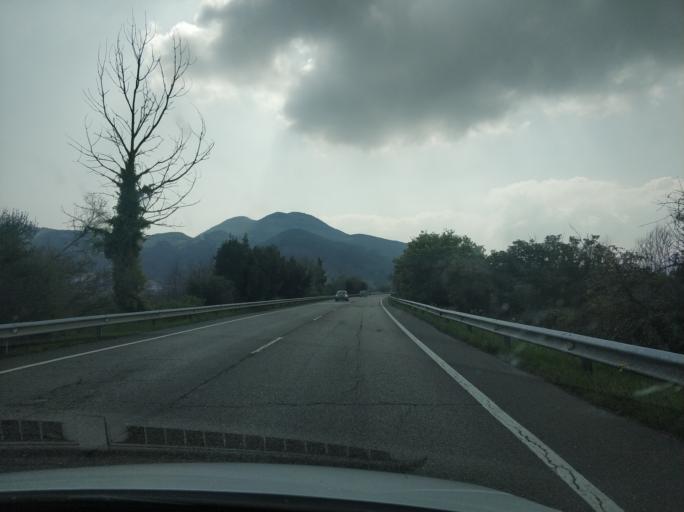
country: ES
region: Cantabria
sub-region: Provincia de Cantabria
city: Santona
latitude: 43.4588
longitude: -3.4664
